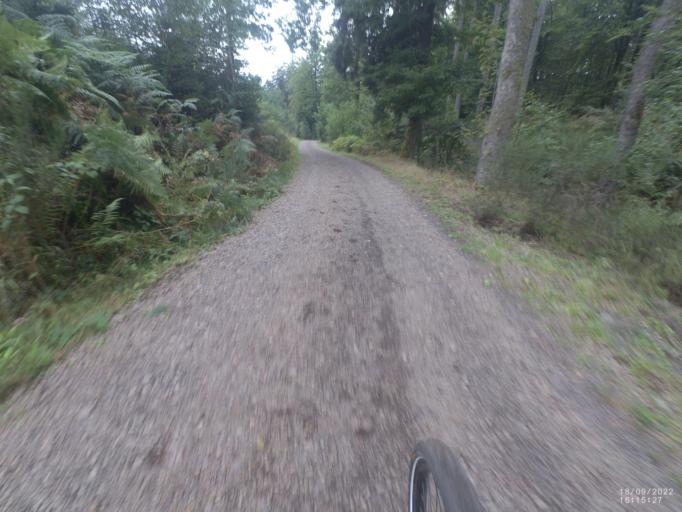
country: DE
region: Rheinland-Pfalz
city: Deudesfeld
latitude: 50.1094
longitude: 6.7211
